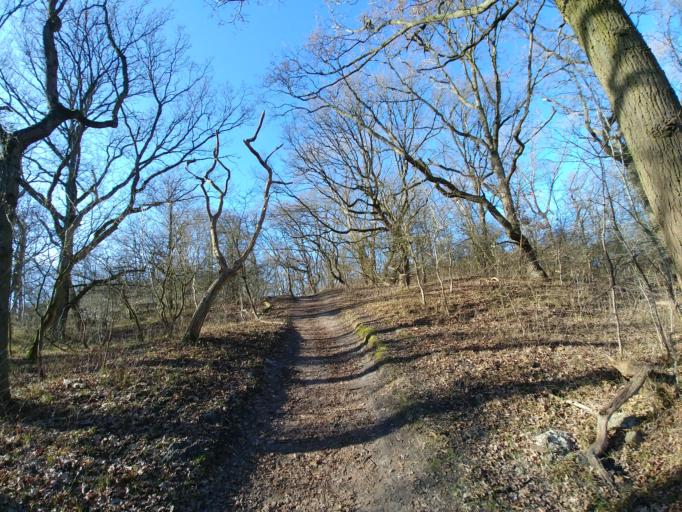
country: NL
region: South Holland
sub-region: Gemeente Den Haag
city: Scheveningen
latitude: 52.1266
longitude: 4.3248
